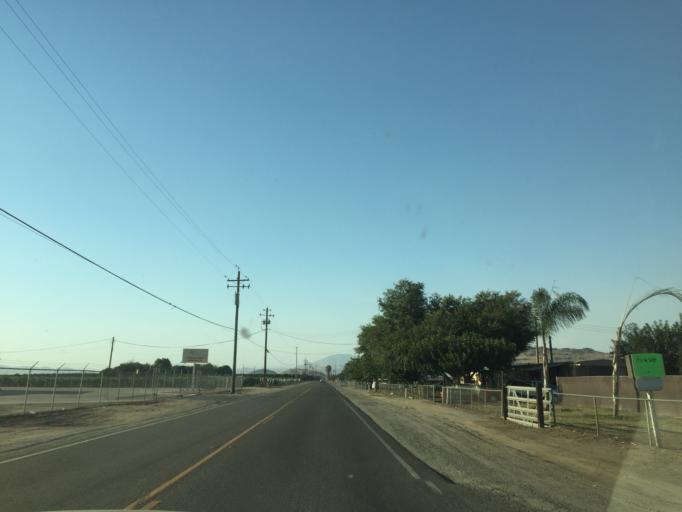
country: US
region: California
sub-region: Tulare County
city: Orosi
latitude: 36.5664
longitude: -119.2871
